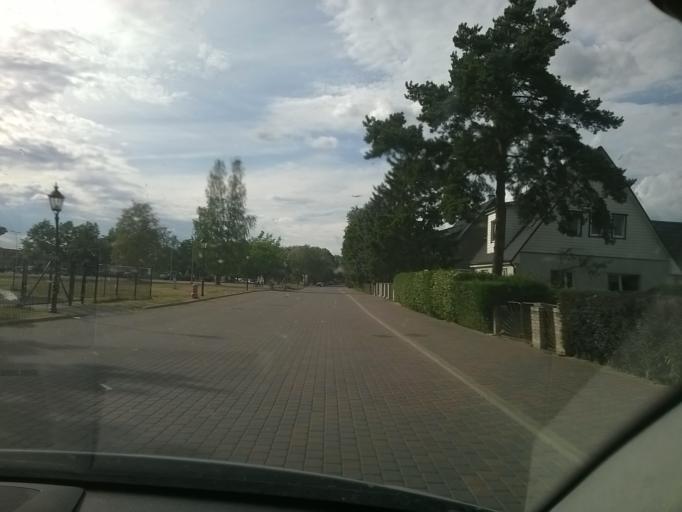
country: EE
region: Vorumaa
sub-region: Voru linn
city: Voru
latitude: 57.8429
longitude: 26.9963
